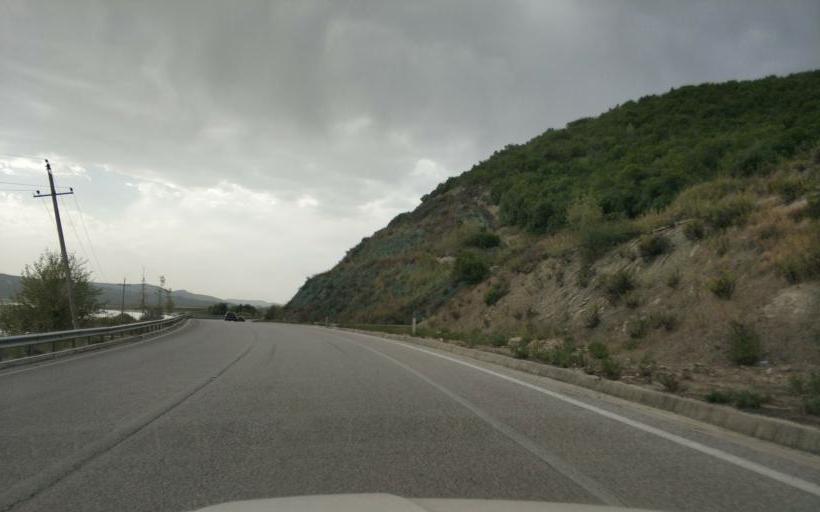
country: AL
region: Fier
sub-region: Rrethi i Mallakastres
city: Hekal
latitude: 40.5298
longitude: 19.7266
